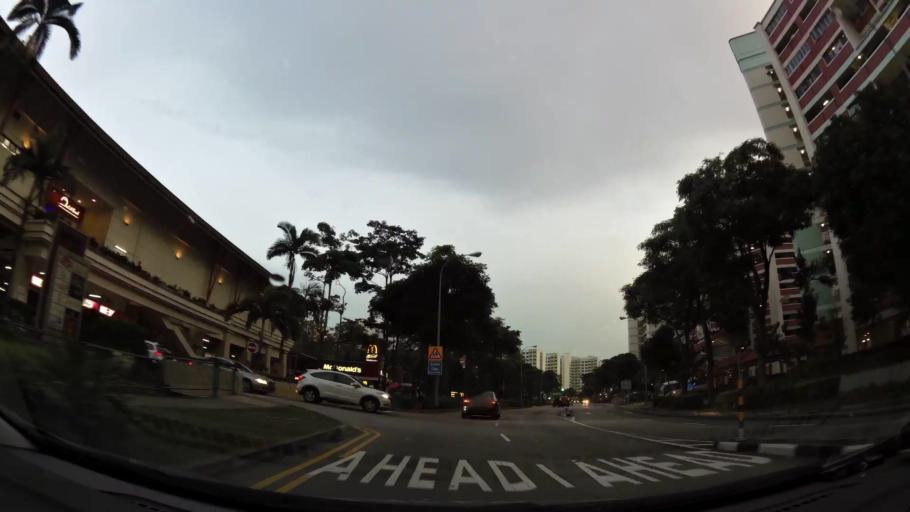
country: MY
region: Johor
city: Kampung Pasir Gudang Baru
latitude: 1.4238
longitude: 103.8405
